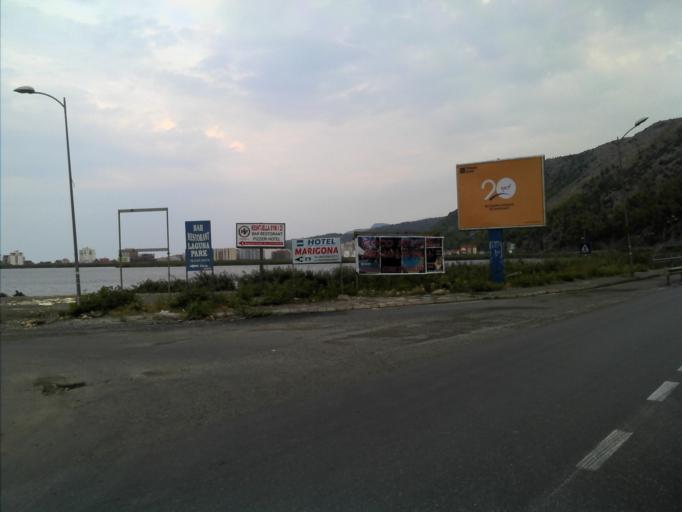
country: AL
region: Lezhe
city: Shengjin
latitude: 41.8010
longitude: 19.6163
